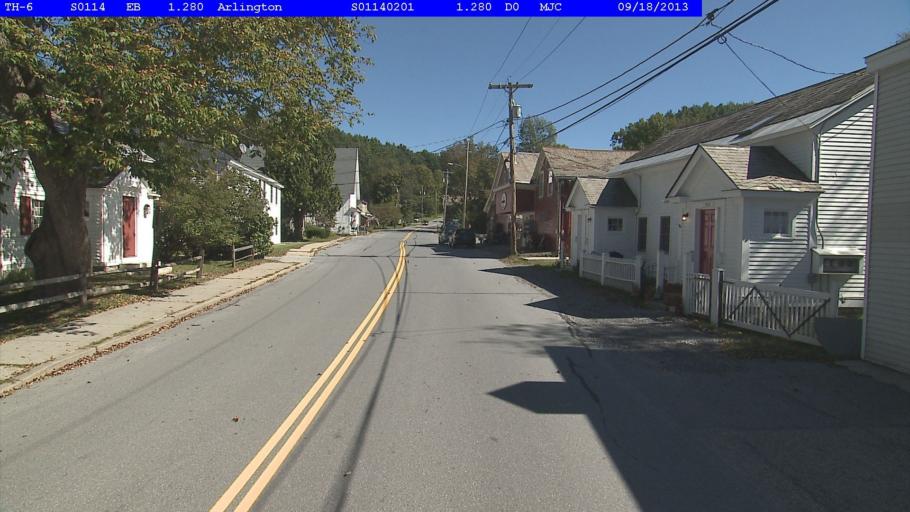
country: US
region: Vermont
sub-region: Bennington County
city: Arlington
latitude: 43.0604
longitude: -73.1417
